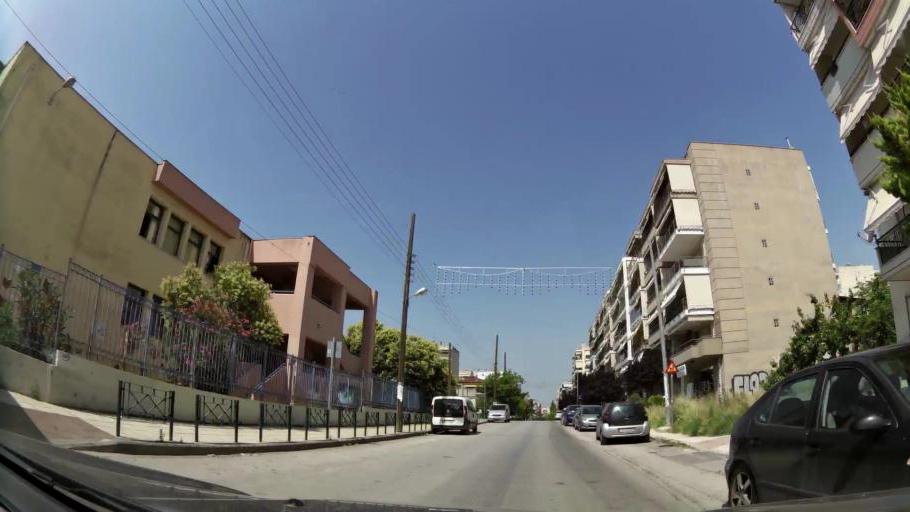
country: GR
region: Central Macedonia
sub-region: Nomos Thessalonikis
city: Evosmos
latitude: 40.6728
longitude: 22.9191
